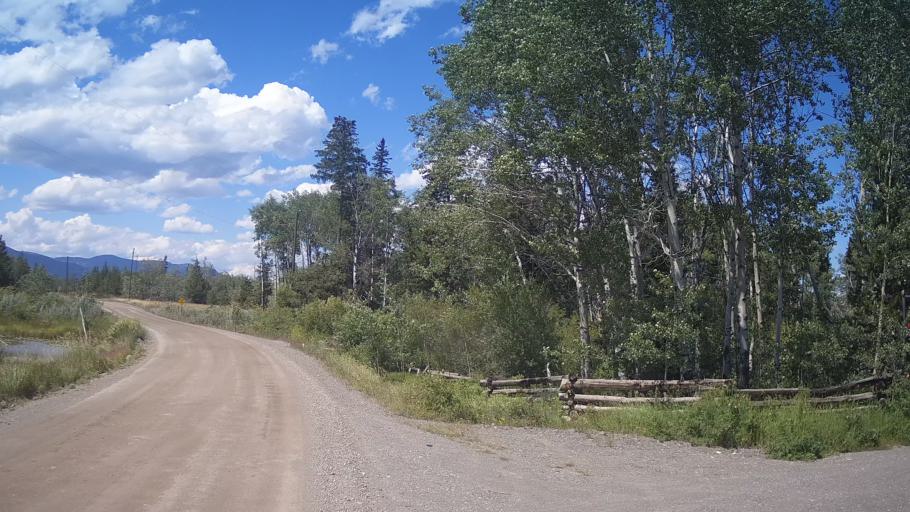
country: CA
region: British Columbia
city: Cache Creek
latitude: 51.2580
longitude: -121.6822
